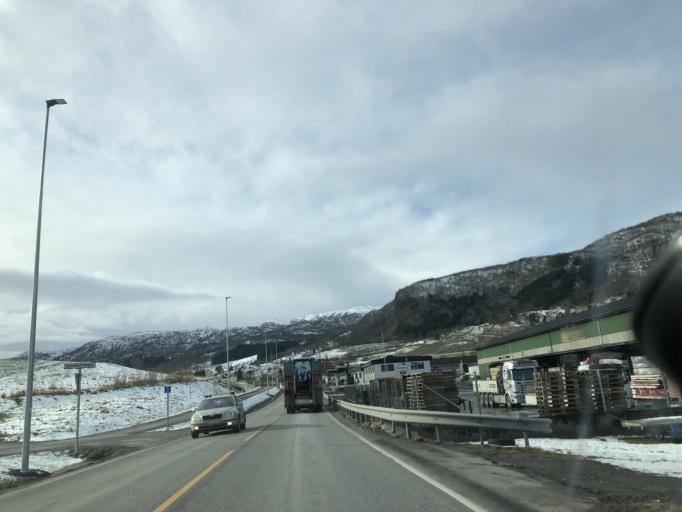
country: NO
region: Rogaland
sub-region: Vindafjord
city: Olen
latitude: 59.5999
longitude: 5.7564
